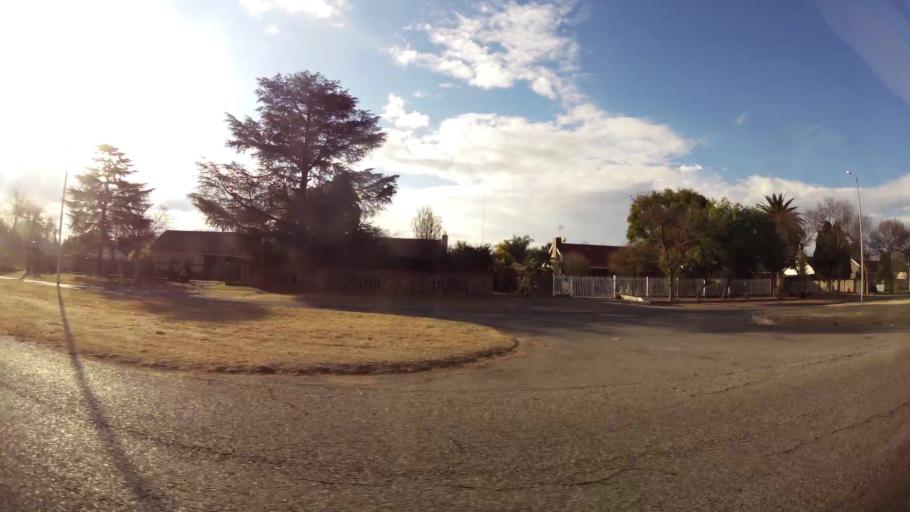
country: ZA
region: Orange Free State
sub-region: Lejweleputswa District Municipality
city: Welkom
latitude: -27.9868
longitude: 26.7187
